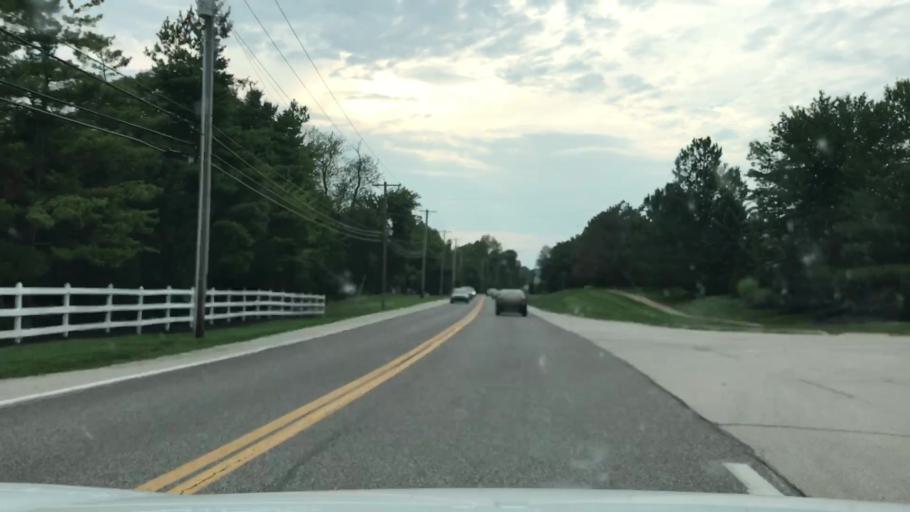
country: US
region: Missouri
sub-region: Saint Louis County
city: Chesterfield
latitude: 38.6563
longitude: -90.6121
